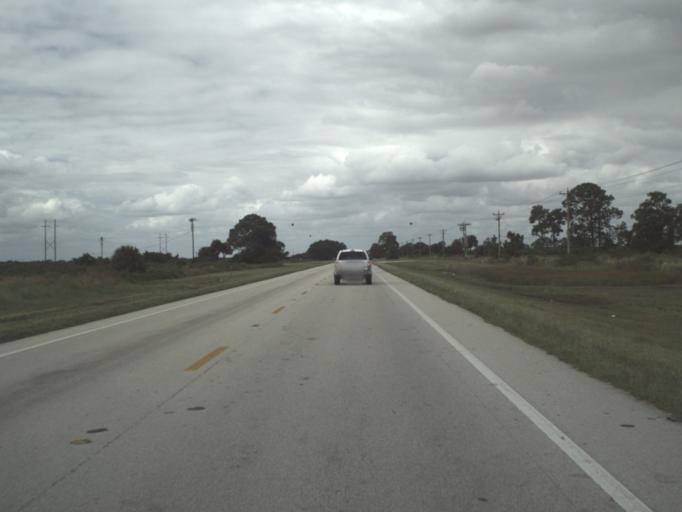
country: US
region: Florida
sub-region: Collier County
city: Immokalee
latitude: 26.4969
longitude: -81.4790
